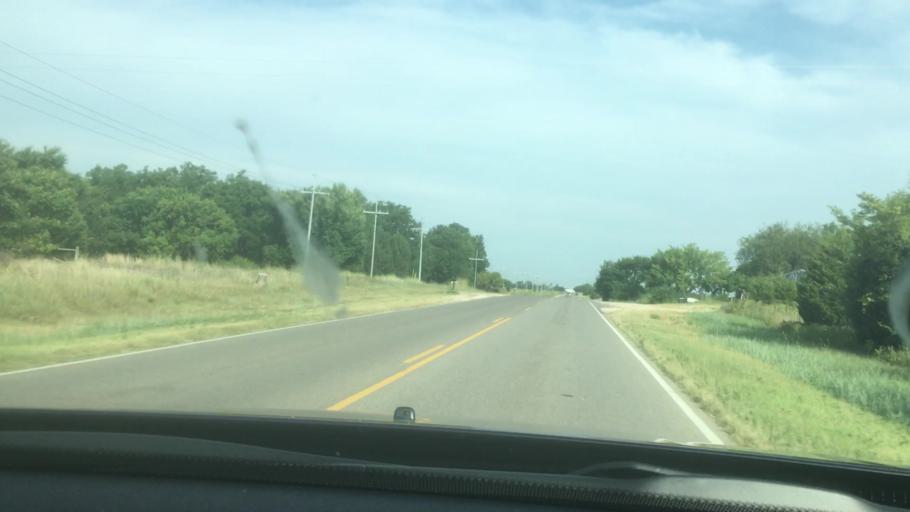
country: US
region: Oklahoma
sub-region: Pontotoc County
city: Ada
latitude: 34.7913
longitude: -96.8050
